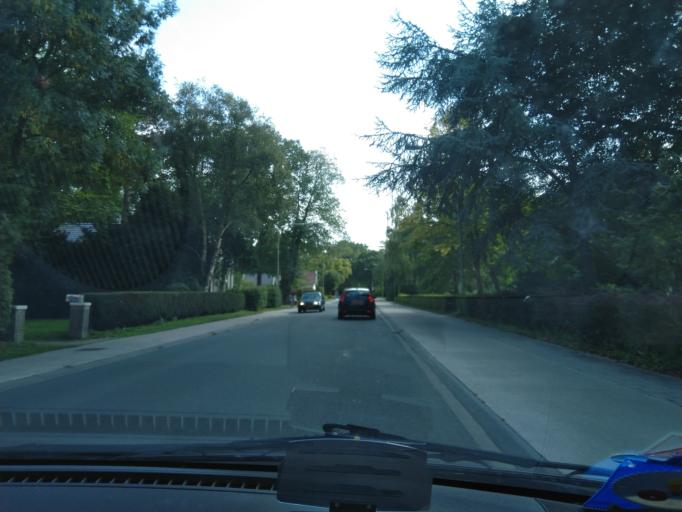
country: NL
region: Groningen
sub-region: Gemeente Haren
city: Haren
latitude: 53.1548
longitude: 6.5647
